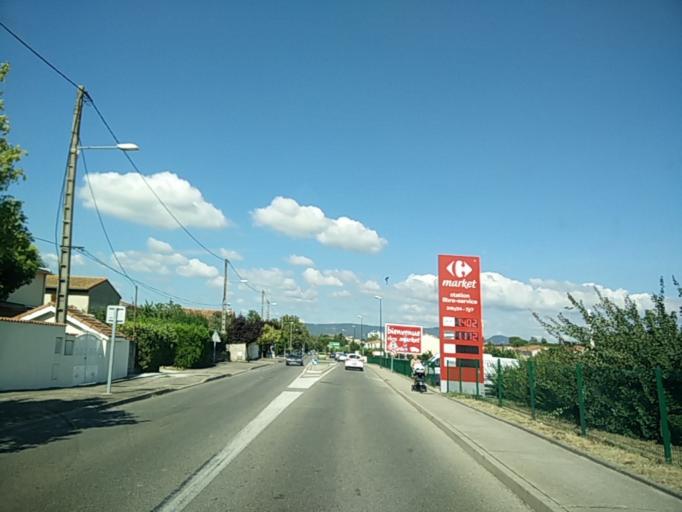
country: FR
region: Rhone-Alpes
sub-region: Departement de la Drome
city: Montelimar
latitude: 44.5509
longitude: 4.7700
